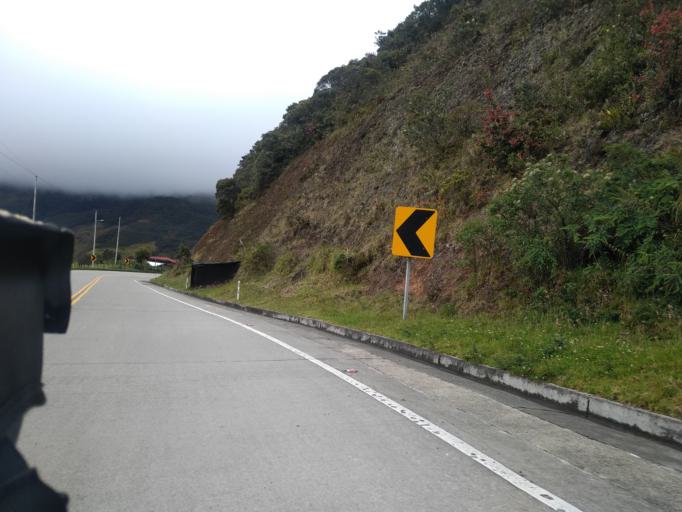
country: EC
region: Loja
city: Catamayo
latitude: -3.8522
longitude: -79.2852
